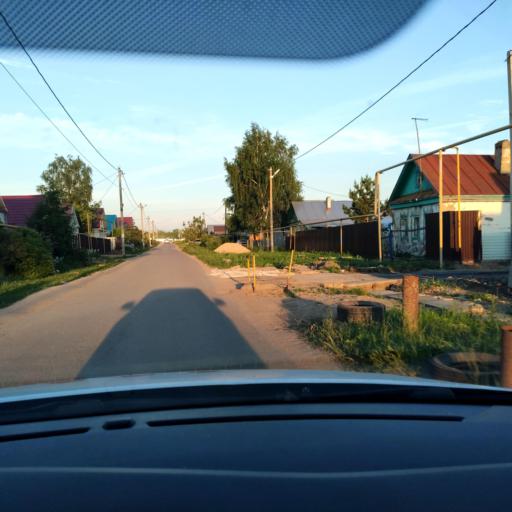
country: RU
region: Tatarstan
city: Stolbishchi
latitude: 55.7482
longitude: 49.3024
